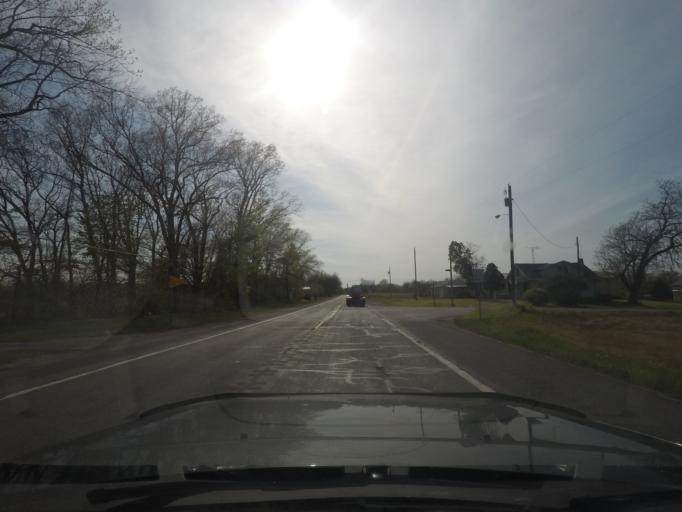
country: US
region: Indiana
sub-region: Saint Joseph County
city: New Carlisle
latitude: 41.7980
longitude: -86.4741
